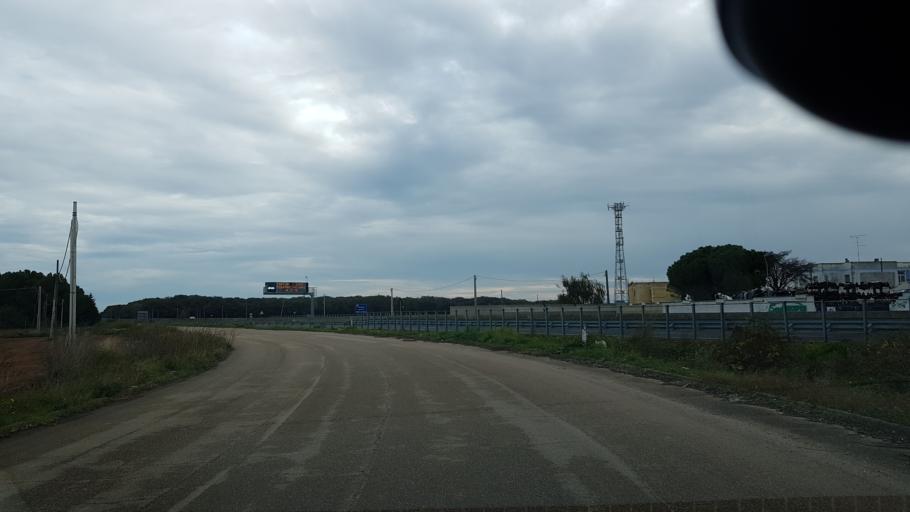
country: IT
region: Apulia
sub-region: Provincia di Brindisi
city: Brindisi
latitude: 40.6648
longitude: 17.8783
